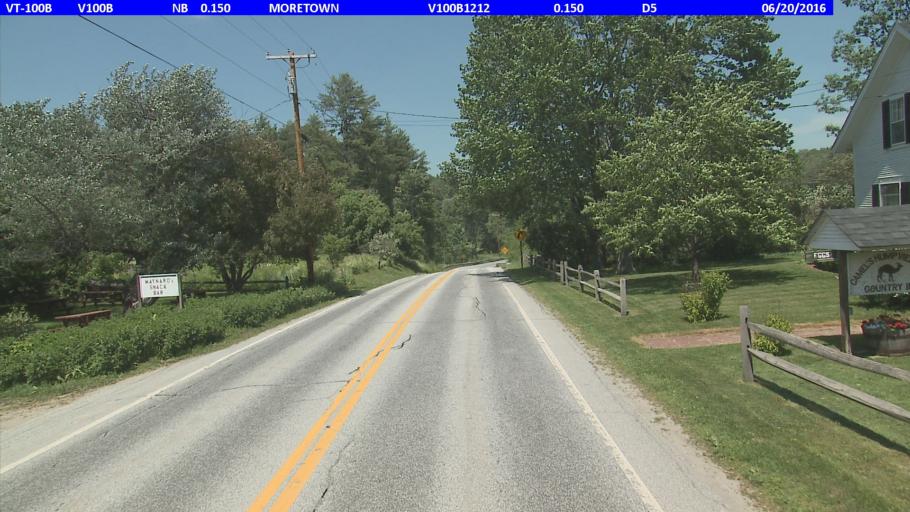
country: US
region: Vermont
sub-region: Washington County
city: Waterbury
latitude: 44.2425
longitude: -72.7753
